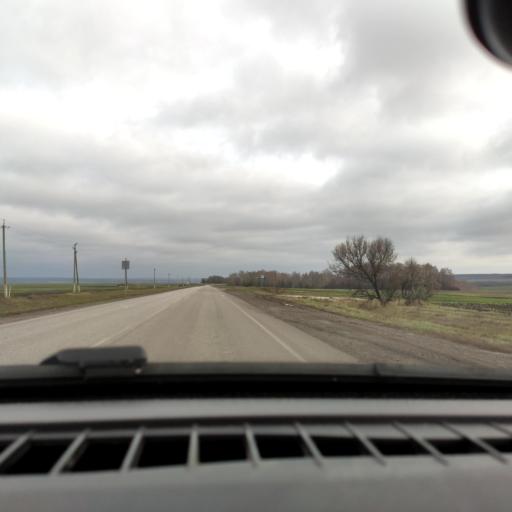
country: RU
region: Belgorod
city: Ilovka
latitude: 50.7529
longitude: 38.7194
